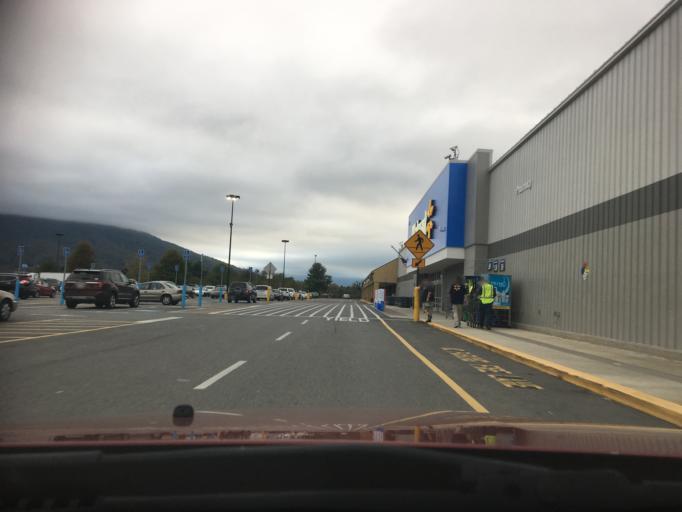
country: US
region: Virginia
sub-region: Giles County
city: Pearisburg
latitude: 37.3289
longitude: -80.7084
